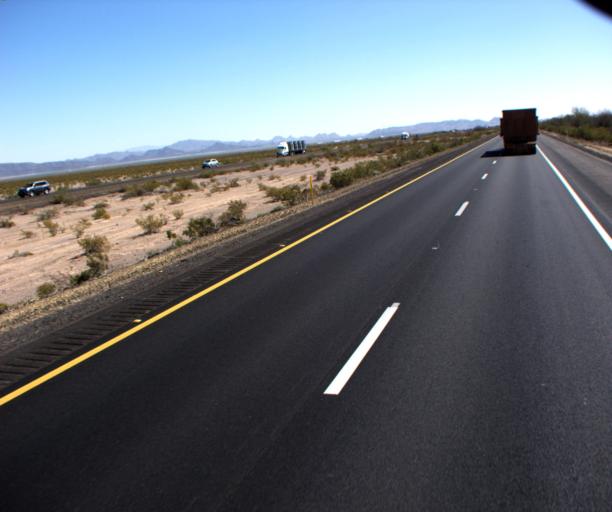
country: US
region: Arizona
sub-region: La Paz County
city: Salome
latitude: 33.6380
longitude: -113.8167
